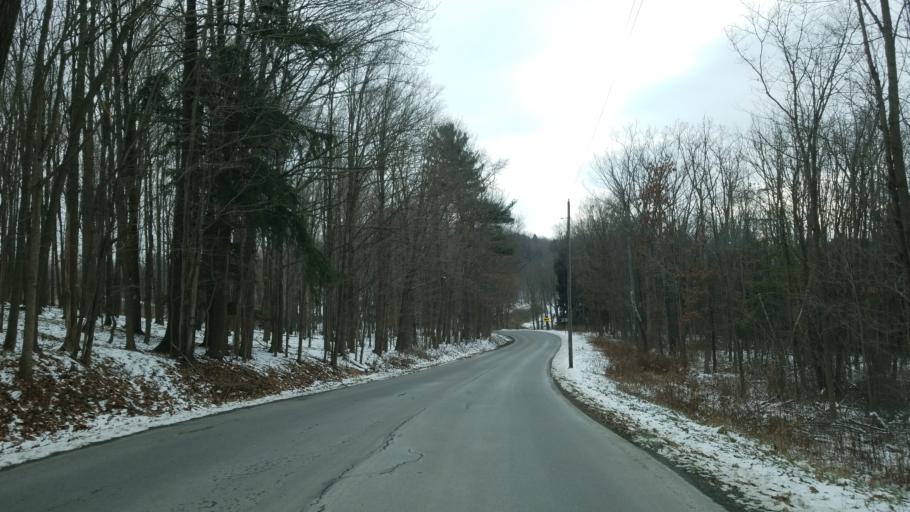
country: US
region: Pennsylvania
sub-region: Clearfield County
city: Sandy
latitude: 41.0921
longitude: -78.7504
